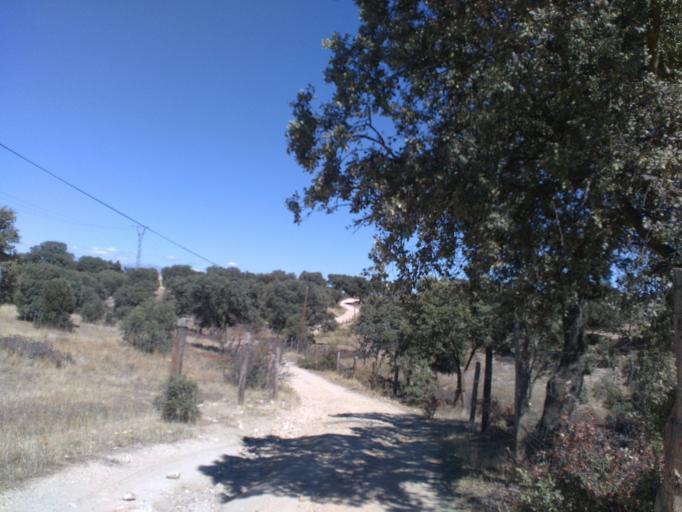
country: ES
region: Madrid
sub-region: Provincia de Madrid
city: Villanueva del Pardillo
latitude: 40.4536
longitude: -3.9581
